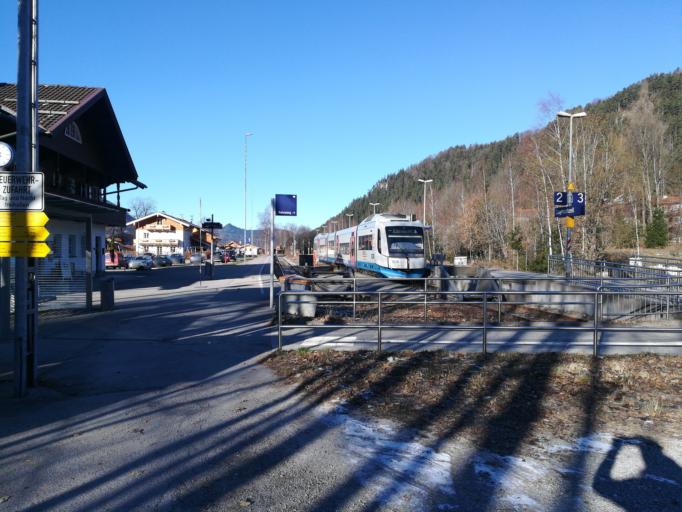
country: DE
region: Bavaria
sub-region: Upper Bavaria
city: Bayrischzell
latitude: 47.6751
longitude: 12.0120
